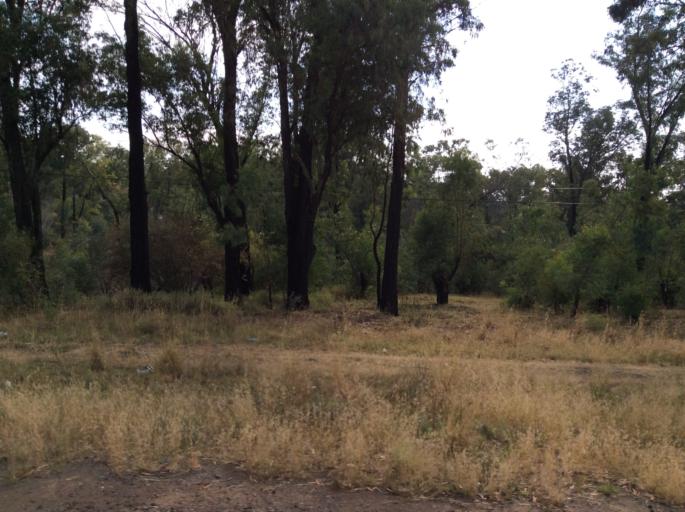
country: ZA
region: Orange Free State
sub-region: Xhariep District Municipality
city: Dewetsdorp
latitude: -29.5790
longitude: 26.6734
